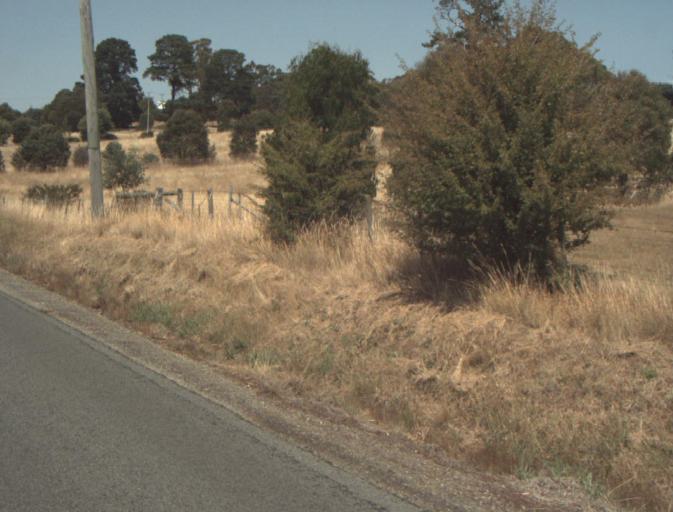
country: AU
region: Tasmania
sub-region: Launceston
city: Newstead
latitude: -41.4927
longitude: 147.2075
